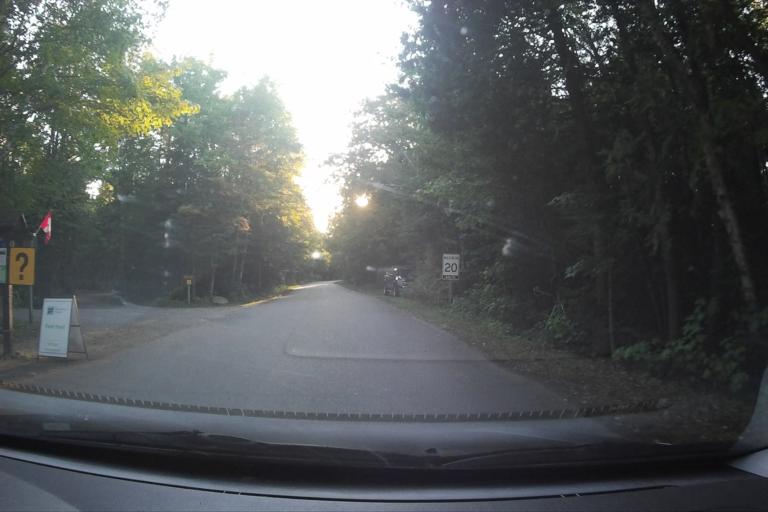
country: CA
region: Ontario
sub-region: Algoma
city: Sault Ste. Marie
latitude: 46.9699
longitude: -84.6948
